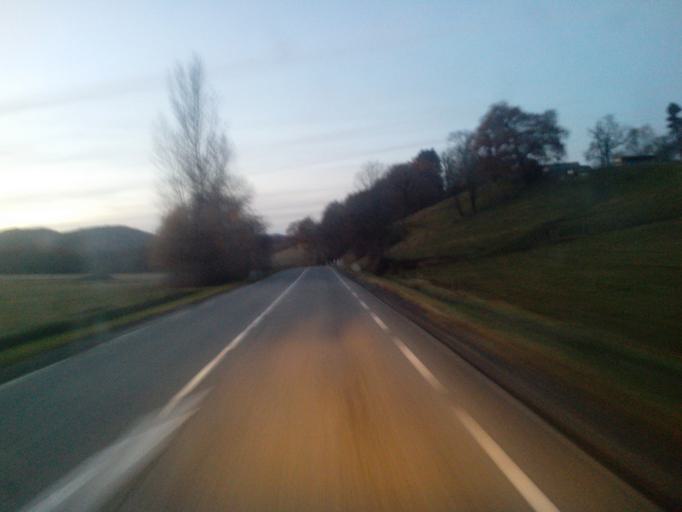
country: FR
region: Midi-Pyrenees
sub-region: Departement de l'Ariege
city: Foix
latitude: 43.0055
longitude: 1.5280
